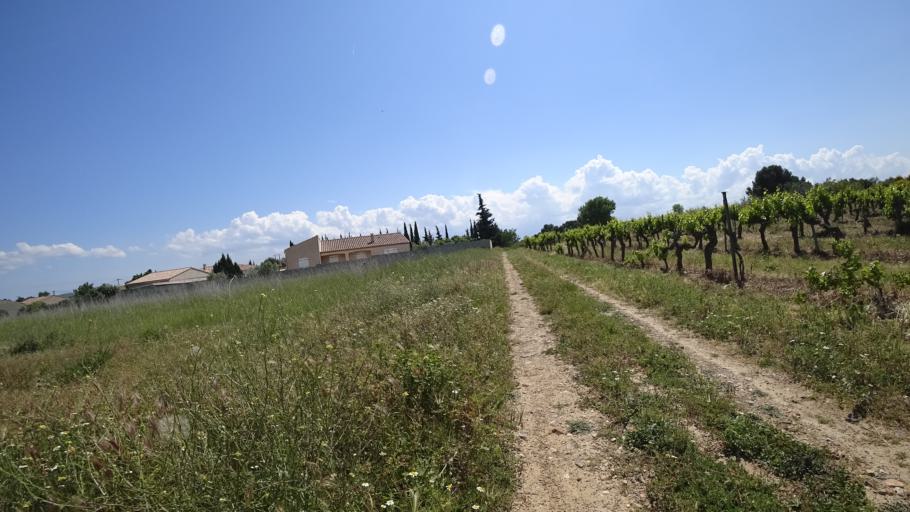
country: FR
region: Languedoc-Roussillon
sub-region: Departement de l'Aude
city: Canet
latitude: 43.2540
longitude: 2.8226
